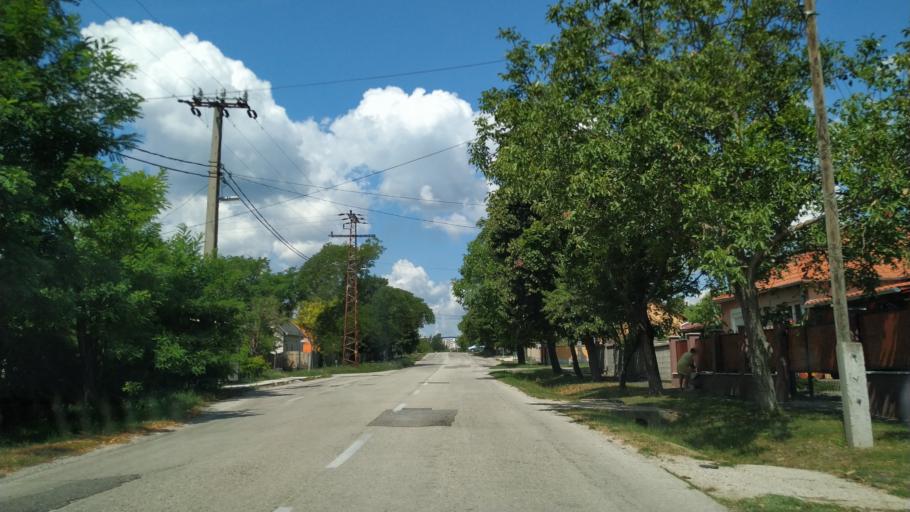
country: HU
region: Veszprem
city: Varpalota
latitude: 47.2017
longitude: 18.1653
